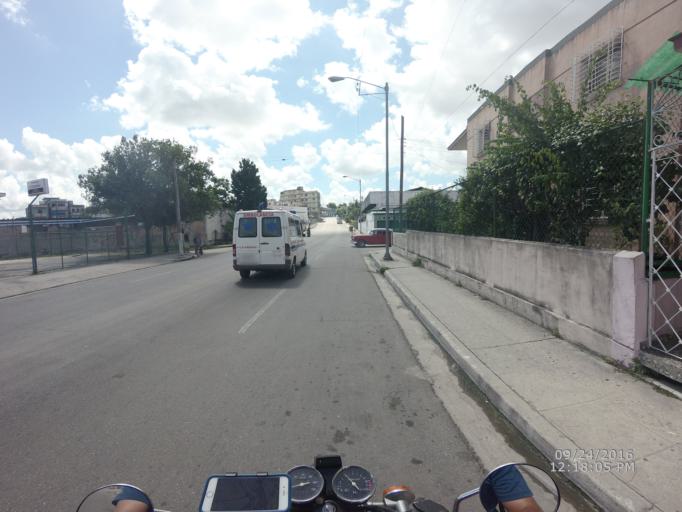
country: CU
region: La Habana
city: Diez de Octubre
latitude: 23.1047
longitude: -82.3510
